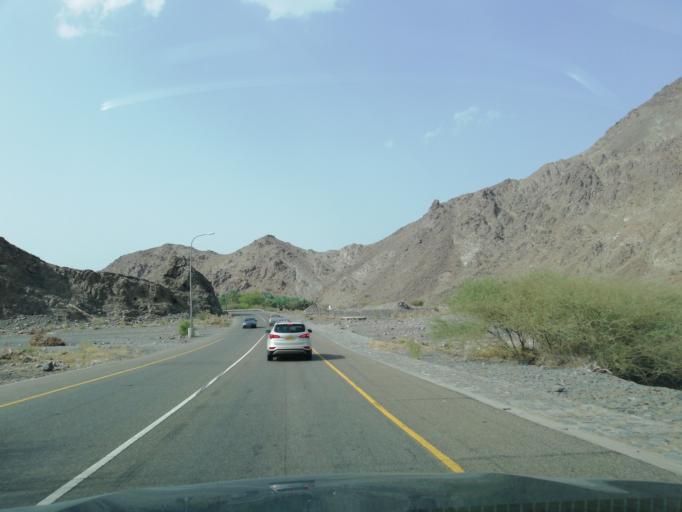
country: OM
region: Muhafazat ad Dakhiliyah
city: Sufalat Sama'il
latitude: 23.2247
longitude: 58.0794
